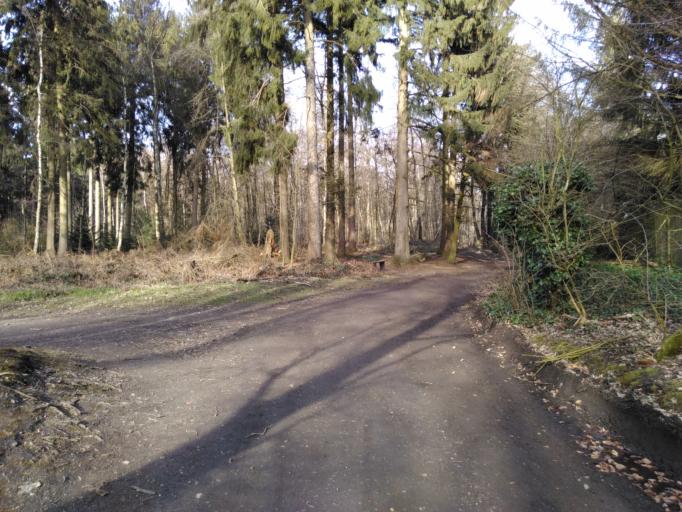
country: NL
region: Limburg
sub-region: Gemeente Vaals
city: Vaals
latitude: 50.7548
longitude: 6.0232
